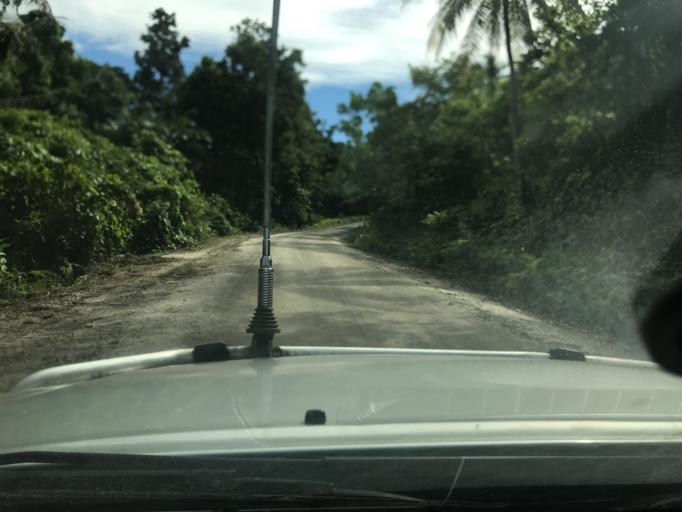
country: SB
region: Malaita
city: Auki
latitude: -8.9147
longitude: 160.7685
